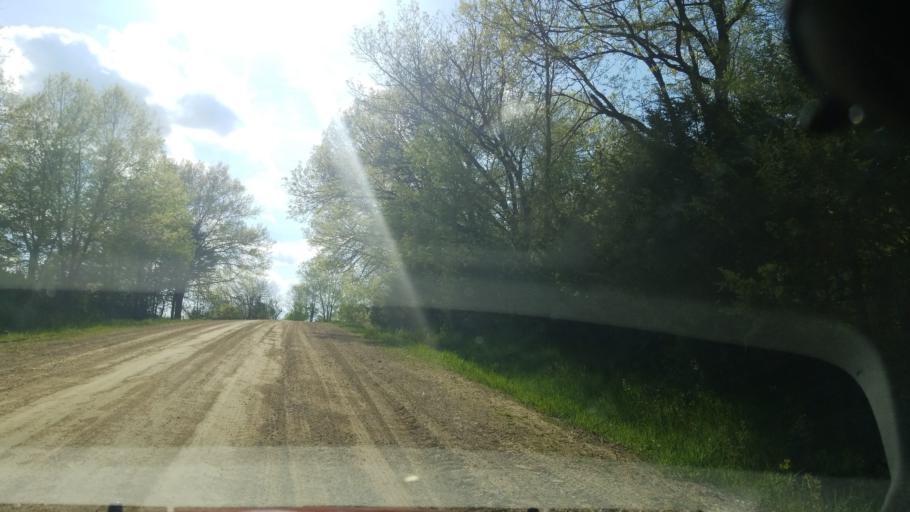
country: US
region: Iowa
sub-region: Jackson County
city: Maquoketa
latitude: 42.1970
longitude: -90.7311
